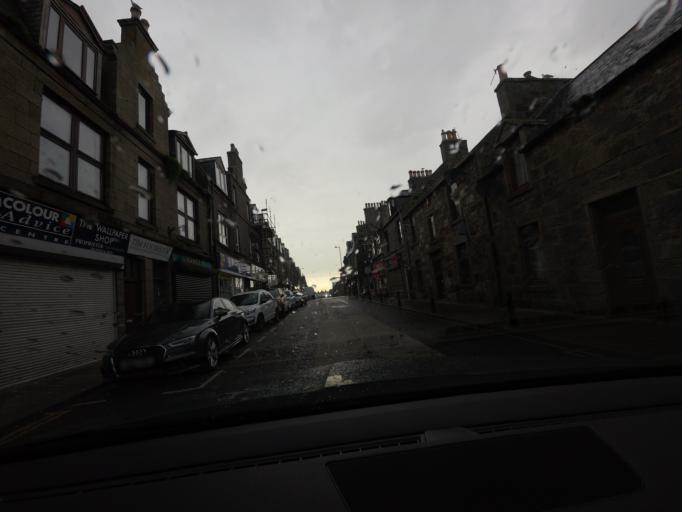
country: GB
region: Scotland
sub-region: Aberdeenshire
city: Fraserburgh
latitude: 57.6939
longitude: -2.0079
